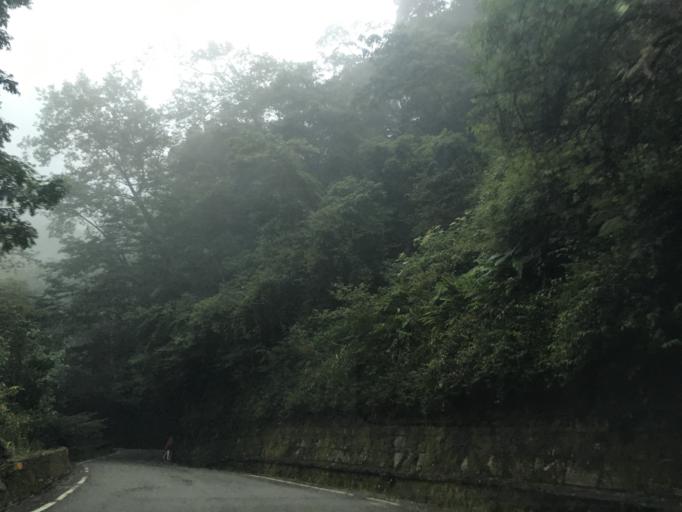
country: TW
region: Taiwan
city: Fengyuan
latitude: 24.2444
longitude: 120.9356
